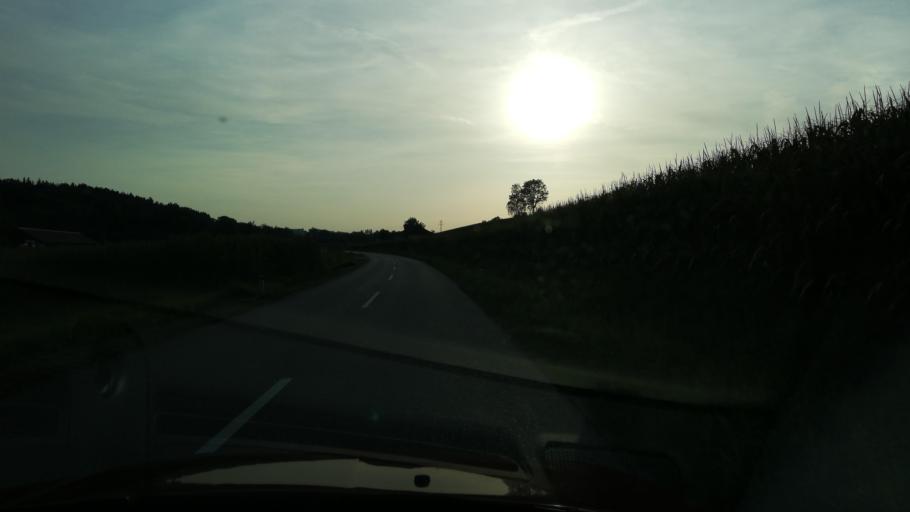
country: AT
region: Upper Austria
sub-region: Wels-Land
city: Edt bei Lambach
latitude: 48.1291
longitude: 13.9071
